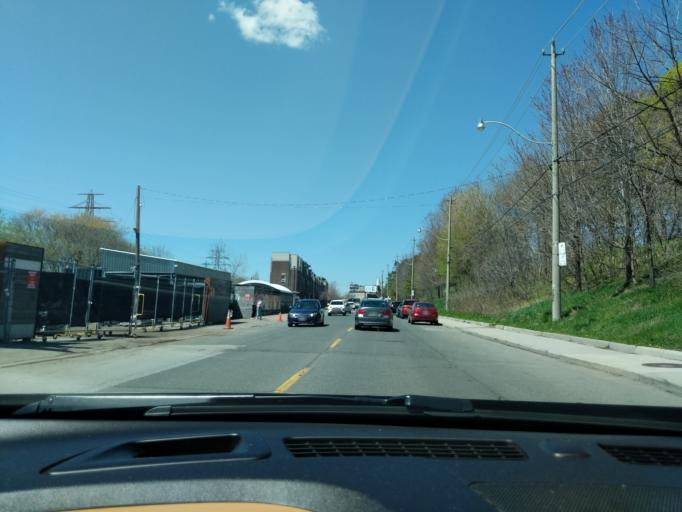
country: CA
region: Ontario
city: Toronto
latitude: 43.6730
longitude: -79.4528
